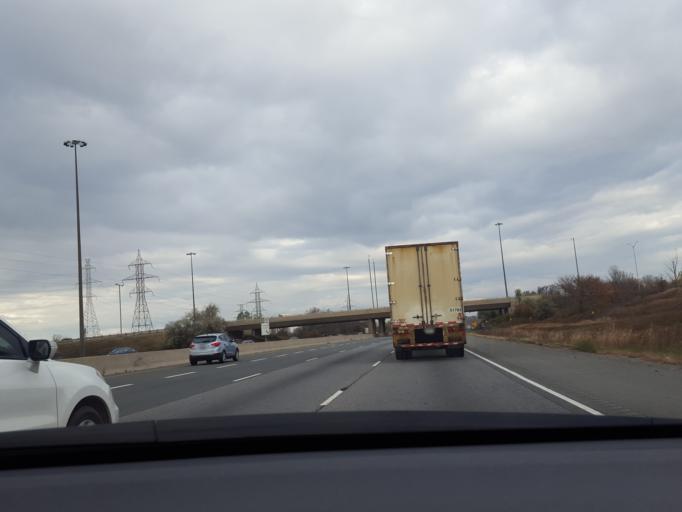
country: CA
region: Ontario
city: Mississauga
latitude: 43.5525
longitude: -79.6983
